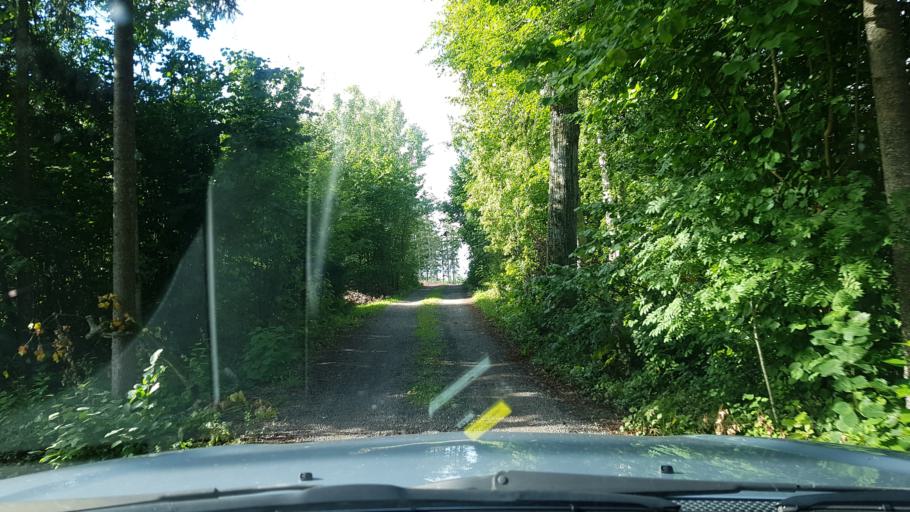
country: EE
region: Harju
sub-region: Rae vald
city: Vaida
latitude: 59.2695
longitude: 25.0240
